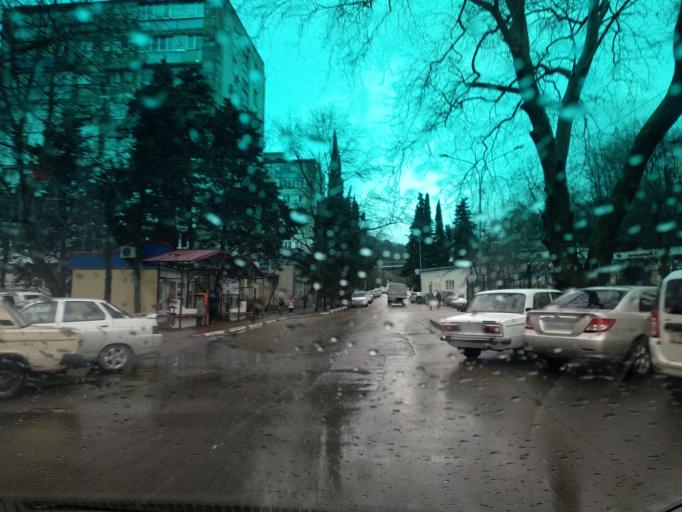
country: RU
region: Krasnodarskiy
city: Tuapse
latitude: 44.1028
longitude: 39.0719
